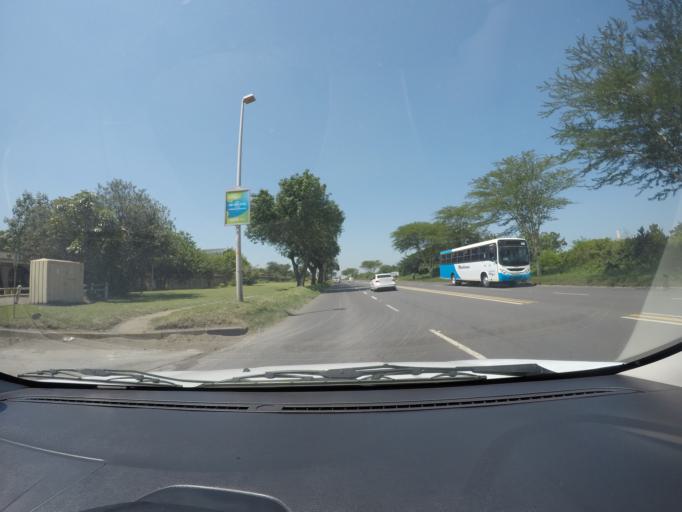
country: ZA
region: KwaZulu-Natal
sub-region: uThungulu District Municipality
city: Richards Bay
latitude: -28.7649
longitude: 32.0192
